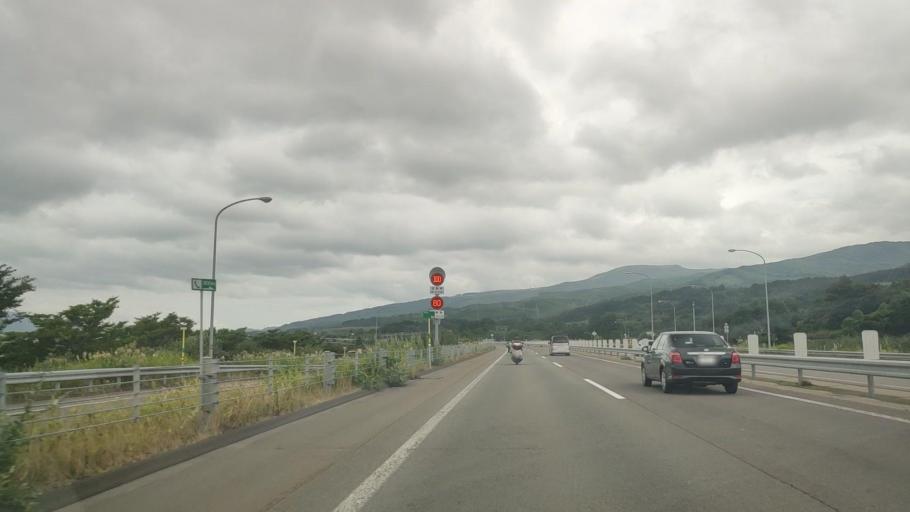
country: JP
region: Hokkaido
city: Nanae
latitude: 41.8666
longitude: 140.7301
